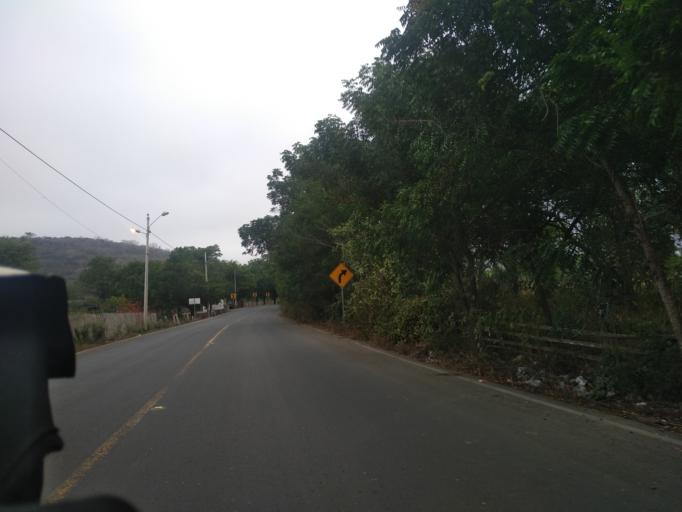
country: EC
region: Manabi
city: Montecristi
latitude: -1.0849
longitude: -80.6827
